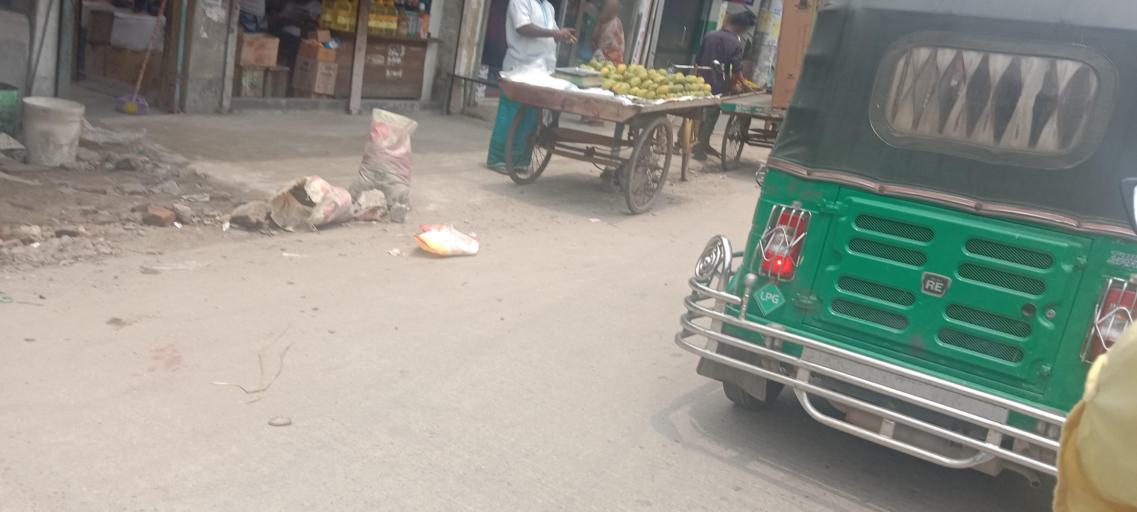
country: BD
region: Dhaka
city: Azimpur
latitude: 23.7300
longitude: 90.3325
